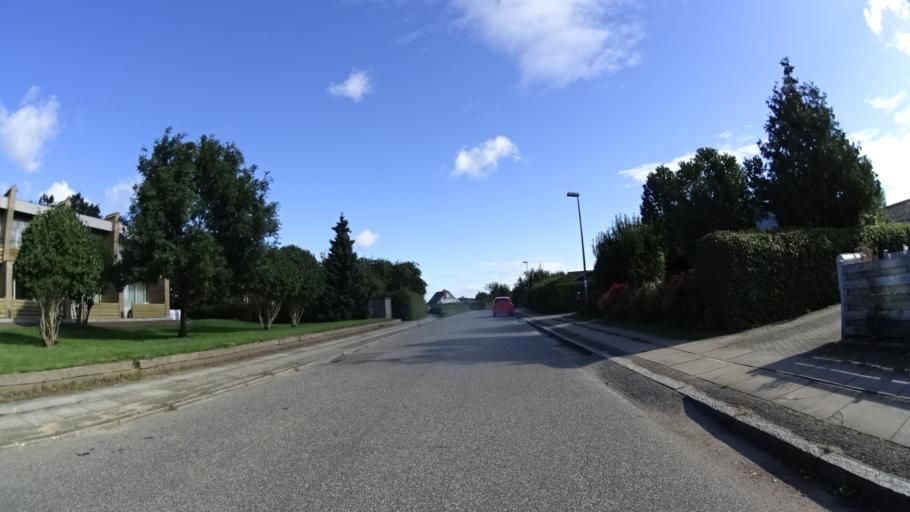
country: DK
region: Central Jutland
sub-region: Arhus Kommune
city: Stavtrup
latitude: 56.1195
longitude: 10.1527
